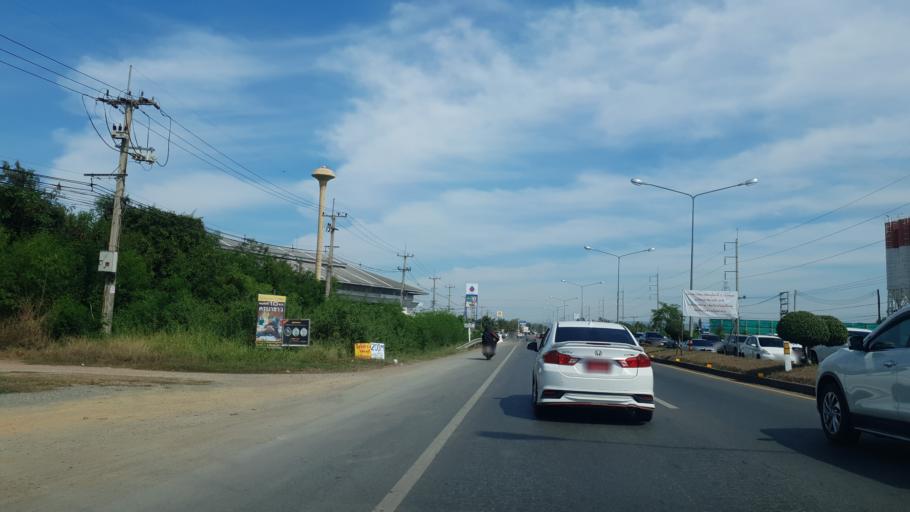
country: TH
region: Phitsanulok
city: Wang Thong
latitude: 16.8546
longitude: 100.3494
